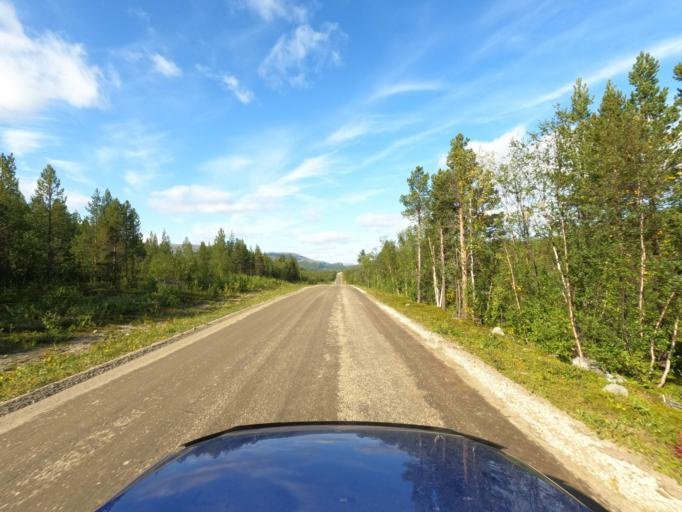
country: NO
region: Finnmark Fylke
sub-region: Porsanger
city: Lakselv
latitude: 69.8736
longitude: 25.0345
